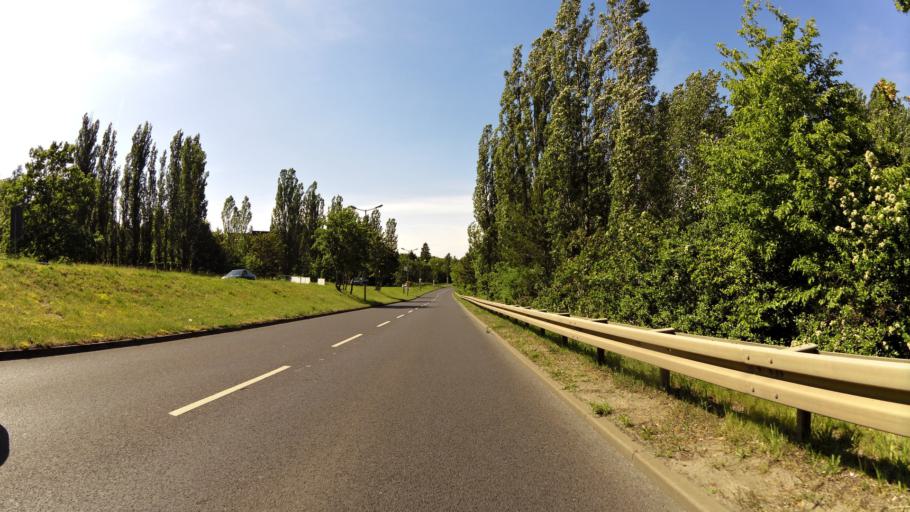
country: DE
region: Brandenburg
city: Frankfurt (Oder)
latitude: 52.3478
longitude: 14.5361
